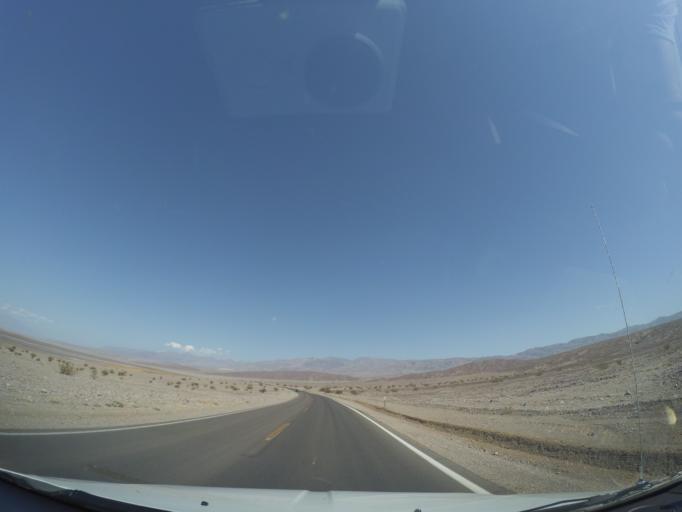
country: US
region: Nevada
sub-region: Nye County
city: Beatty
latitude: 36.5301
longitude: -116.8826
